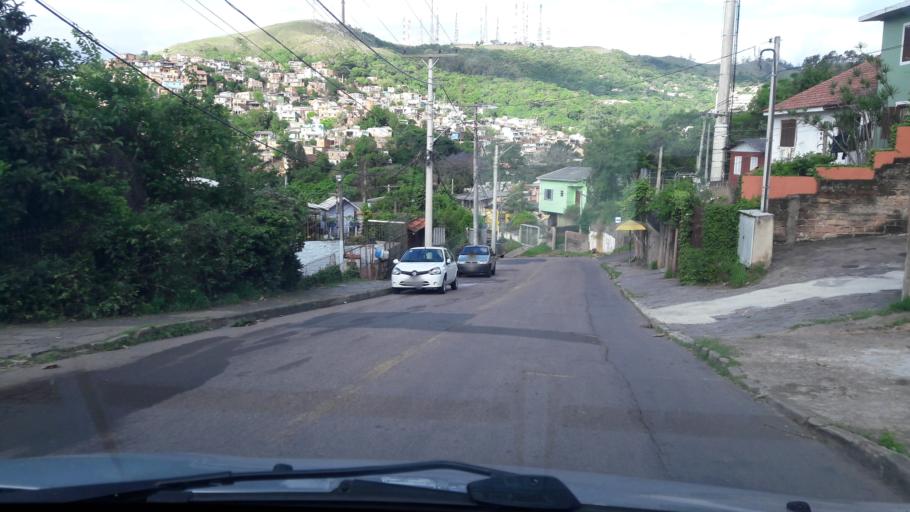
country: BR
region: Rio Grande do Sul
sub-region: Porto Alegre
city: Porto Alegre
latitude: -30.0843
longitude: -51.1988
